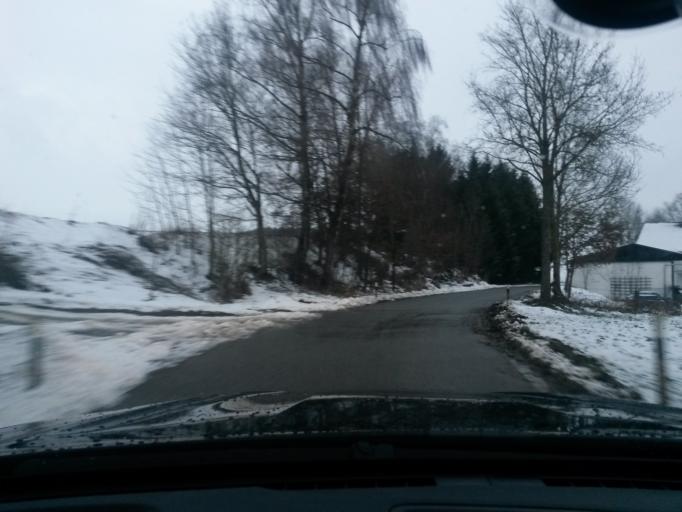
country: DE
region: Bavaria
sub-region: Lower Bavaria
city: Tiefenbach
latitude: 48.4726
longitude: 12.0885
